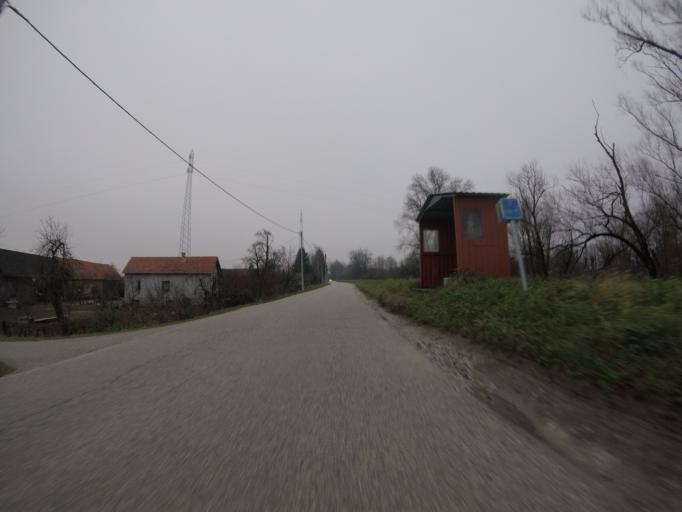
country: HR
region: Sisacko-Moslavacka
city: Lekenik
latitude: 45.6744
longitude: 16.2454
